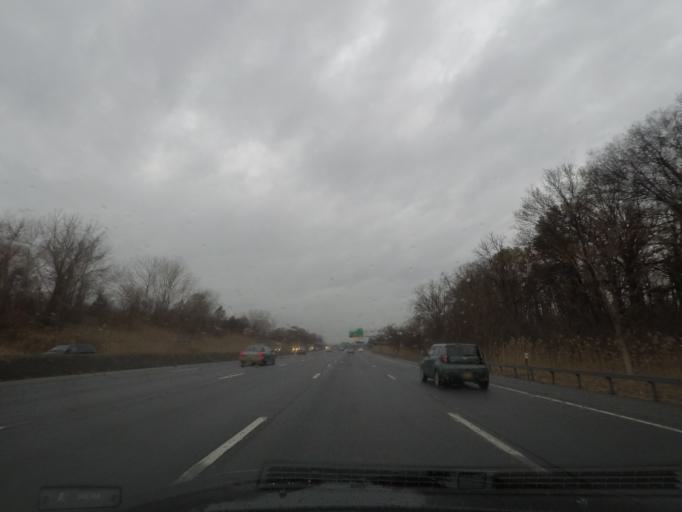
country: US
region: New York
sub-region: Albany County
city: Roessleville
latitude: 42.6892
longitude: -73.8151
